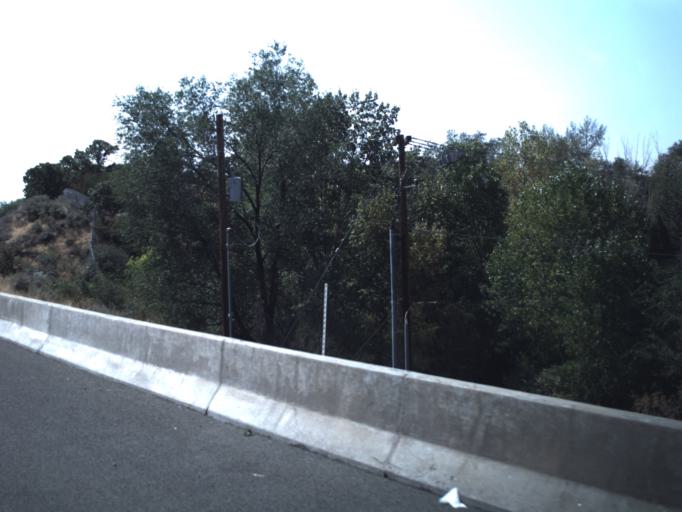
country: US
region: Utah
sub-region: Salt Lake County
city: Cottonwood Heights
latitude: 40.6354
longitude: -111.8113
